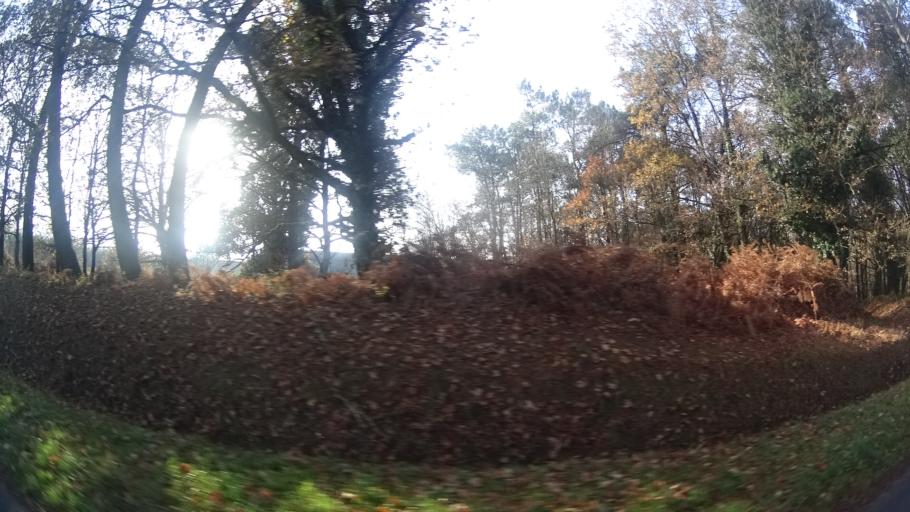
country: FR
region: Brittany
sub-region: Departement du Morbihan
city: Rieux
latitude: 47.5979
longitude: -2.1355
